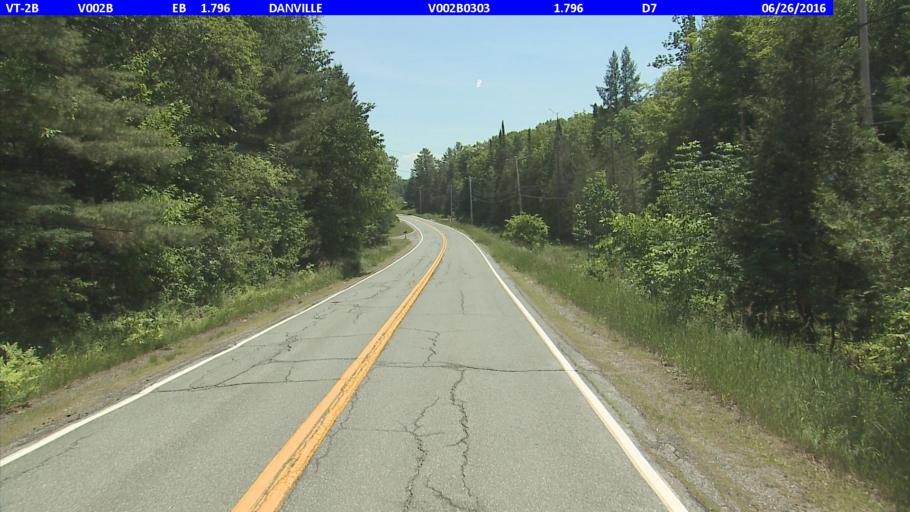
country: US
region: Vermont
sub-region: Caledonia County
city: St Johnsbury
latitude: 44.4303
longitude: -72.0581
